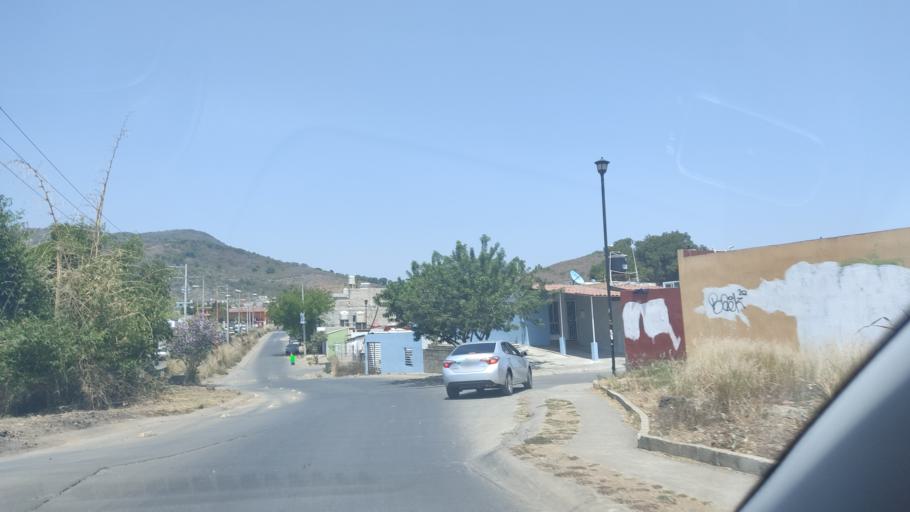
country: MX
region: Nayarit
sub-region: Tepic
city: La Corregidora
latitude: 21.4948
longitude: -104.8220
